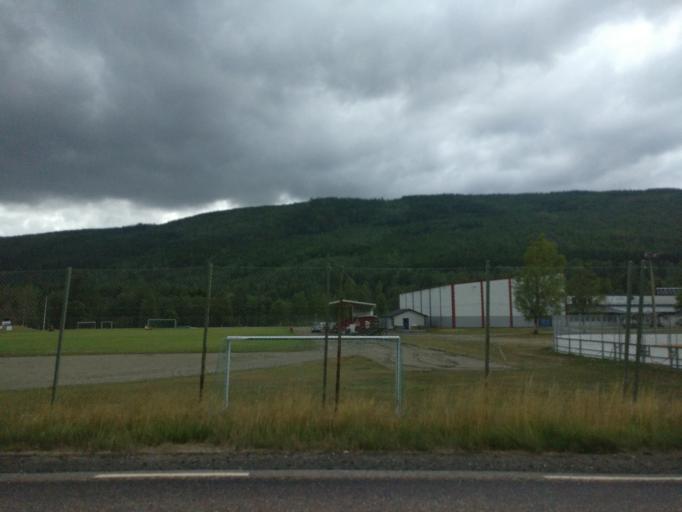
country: SE
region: Vaermland
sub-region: Torsby Kommun
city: Torsby
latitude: 60.7108
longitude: 12.8880
